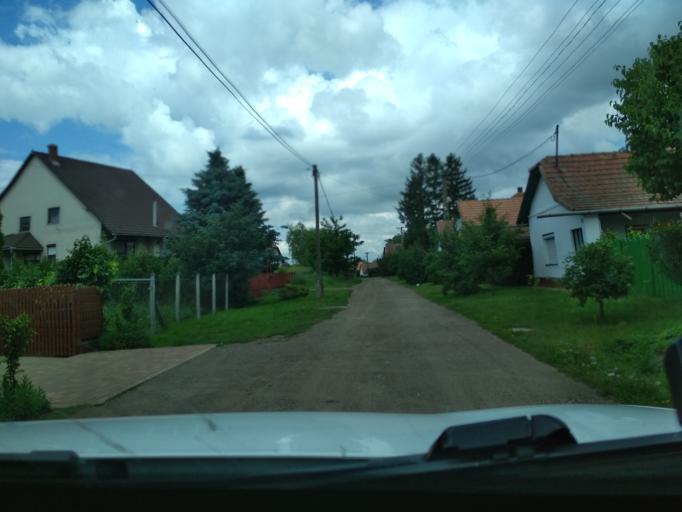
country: HU
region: Jasz-Nagykun-Szolnok
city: Tiszafured
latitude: 47.6105
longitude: 20.7464
